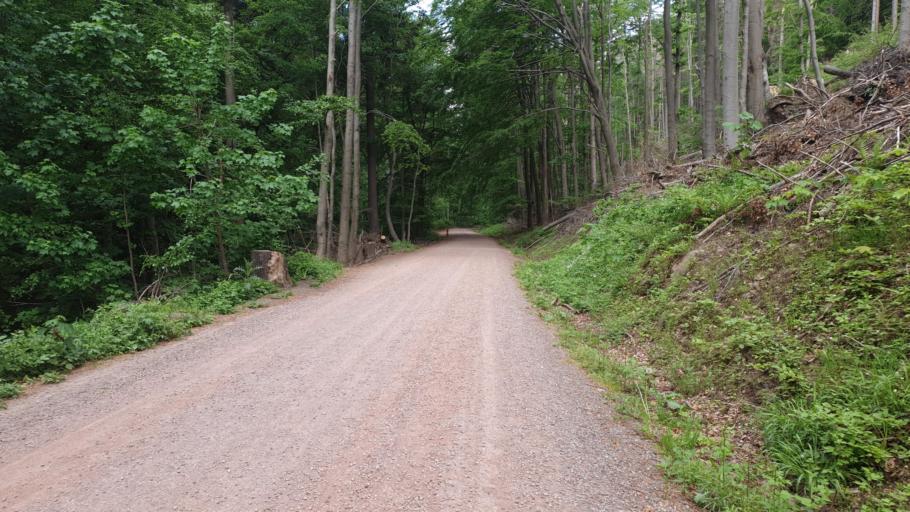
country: DE
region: Saxony-Anhalt
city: Ilsenburg
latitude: 51.8439
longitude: 10.6553
